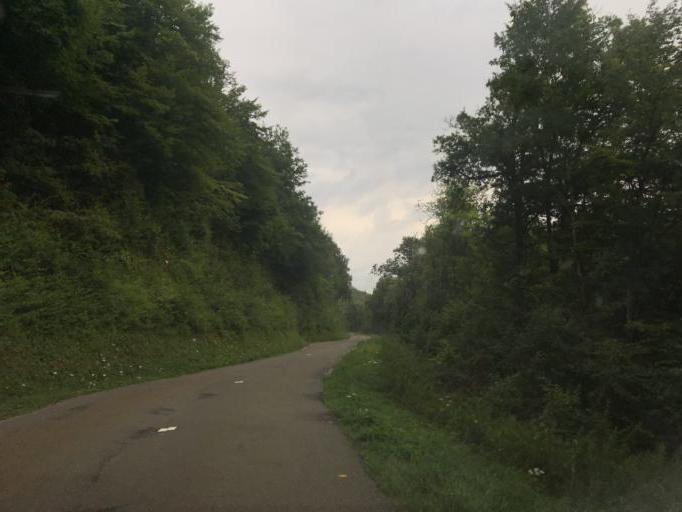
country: FR
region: Franche-Comte
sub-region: Departement du Jura
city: Lavans-les-Saint-Claude
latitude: 46.3307
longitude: 5.7623
